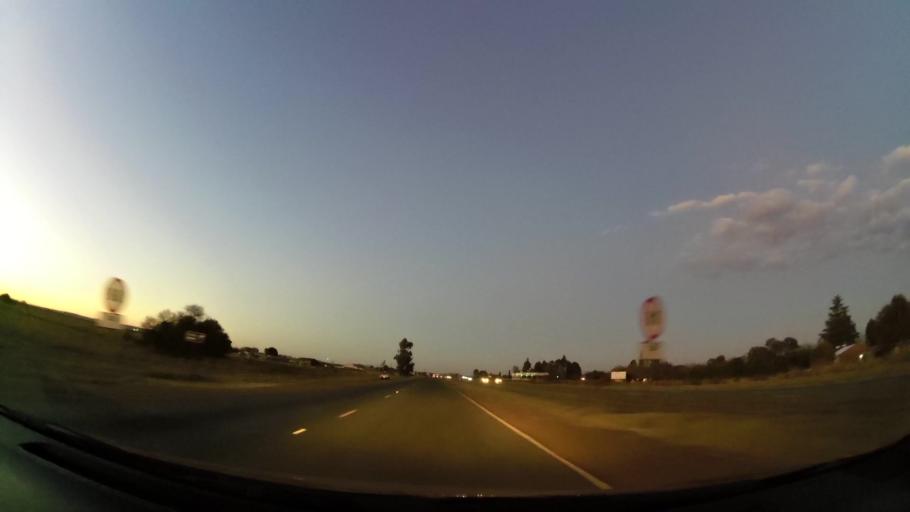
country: ZA
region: North-West
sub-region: Dr Kenneth Kaunda District Municipality
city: Potchefstroom
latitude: -26.7037
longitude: 27.1258
